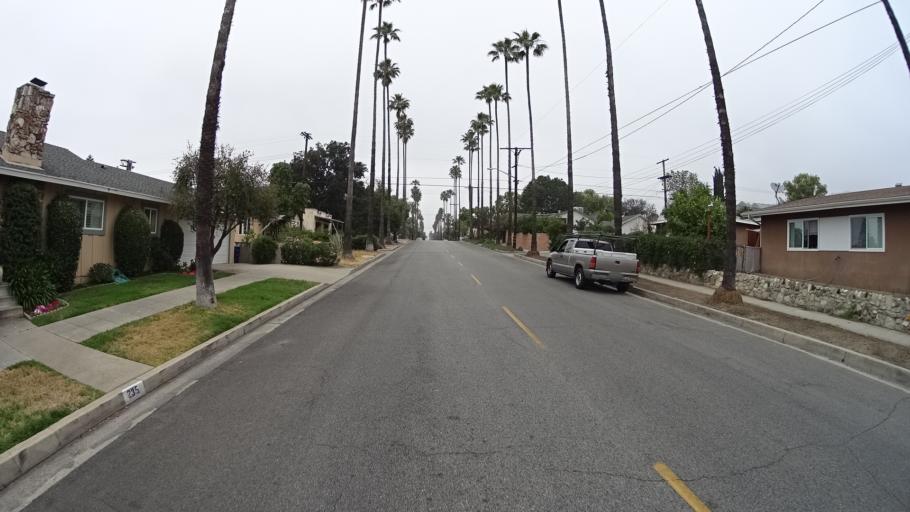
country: US
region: California
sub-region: Los Angeles County
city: Burbank
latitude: 34.1888
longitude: -118.2972
